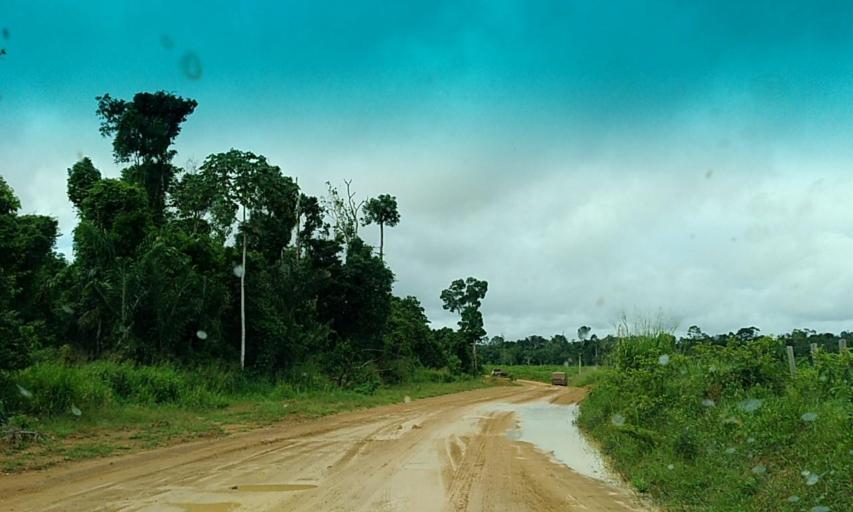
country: BR
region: Para
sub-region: Altamira
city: Altamira
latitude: -3.0683
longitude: -51.7111
